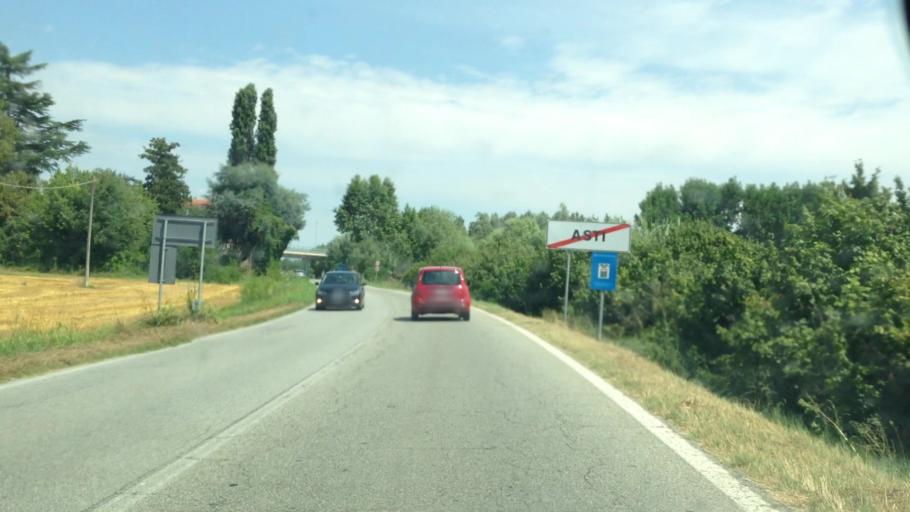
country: IT
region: Piedmont
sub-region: Provincia di Asti
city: Asti
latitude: 44.9212
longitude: 8.2262
